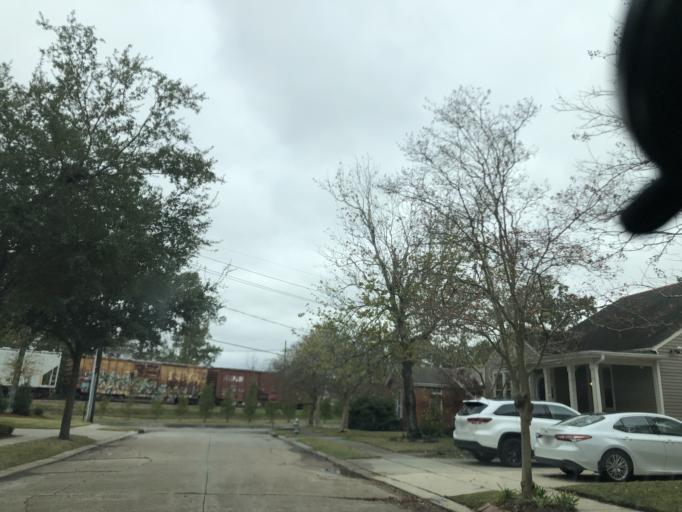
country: US
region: Louisiana
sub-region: Jefferson Parish
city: Metairie
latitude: 29.9777
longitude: -90.1502
